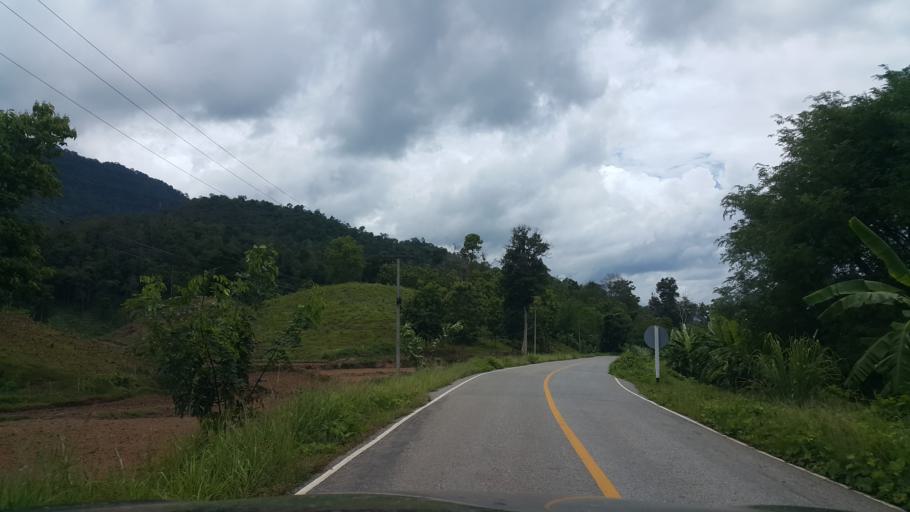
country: TH
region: Phitsanulok
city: Chat Trakan
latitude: 17.3892
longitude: 100.7577
